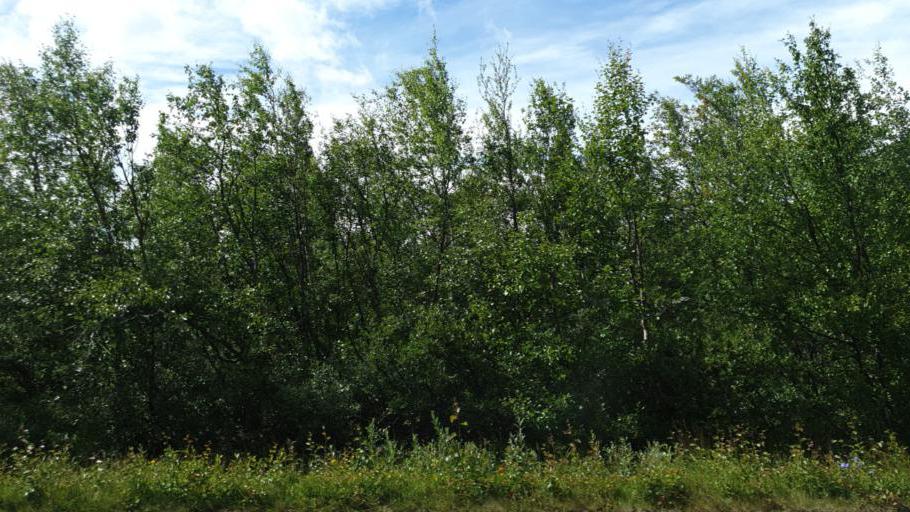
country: NO
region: Oppland
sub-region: Oystre Slidre
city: Heggenes
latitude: 61.4892
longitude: 8.8249
